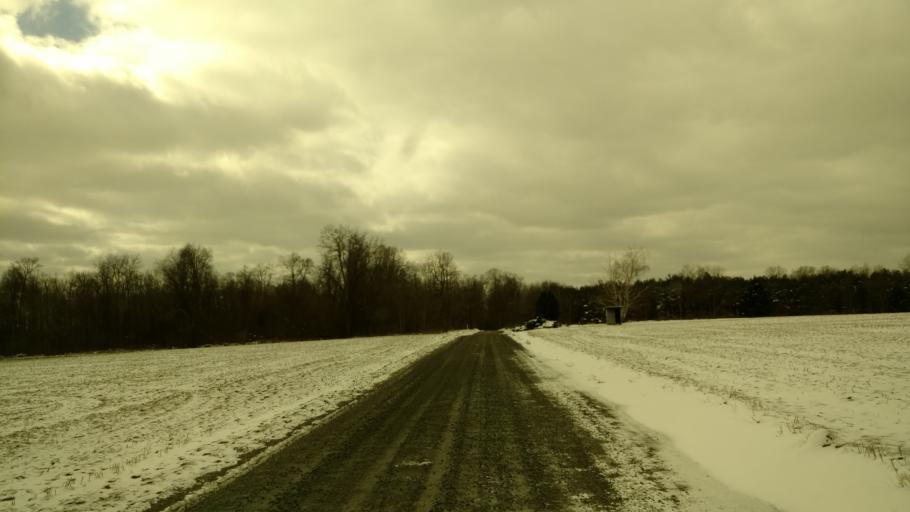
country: US
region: Pennsylvania
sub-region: Mercer County
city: Mercer
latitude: 41.3390
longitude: -80.2376
